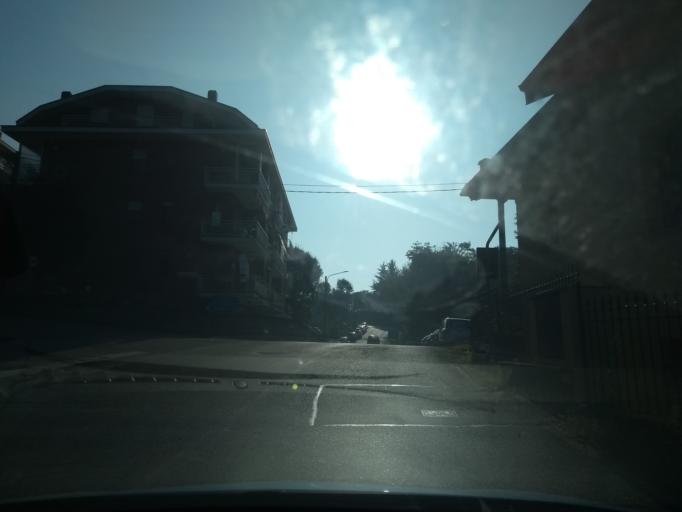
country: IT
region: Piedmont
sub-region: Provincia di Torino
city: Fiano
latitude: 45.2153
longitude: 7.5193
